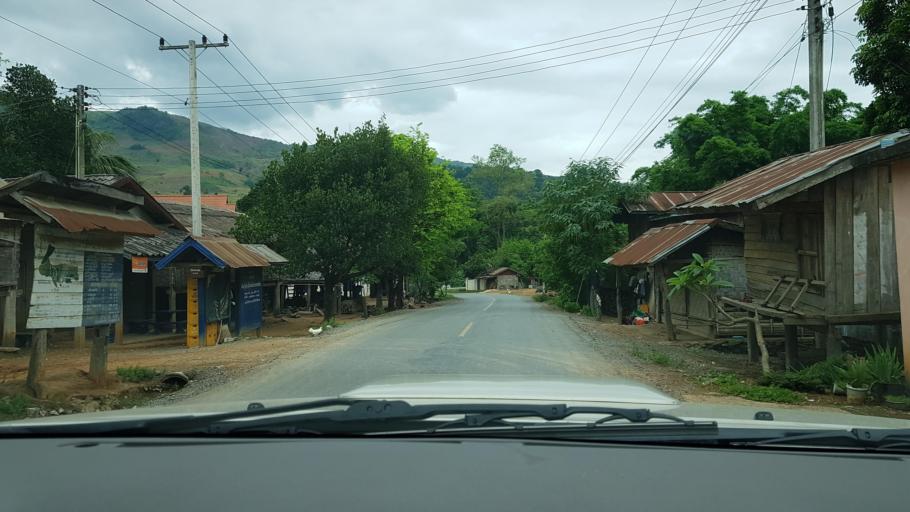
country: LA
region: Loungnamtha
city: Muang Nale
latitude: 20.1873
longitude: 101.5185
